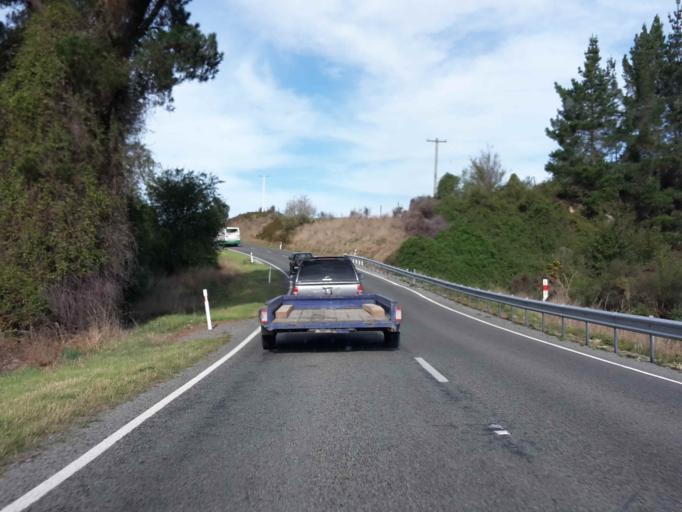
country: NZ
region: Canterbury
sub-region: Timaru District
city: Pleasant Point
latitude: -44.0841
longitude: 170.9808
